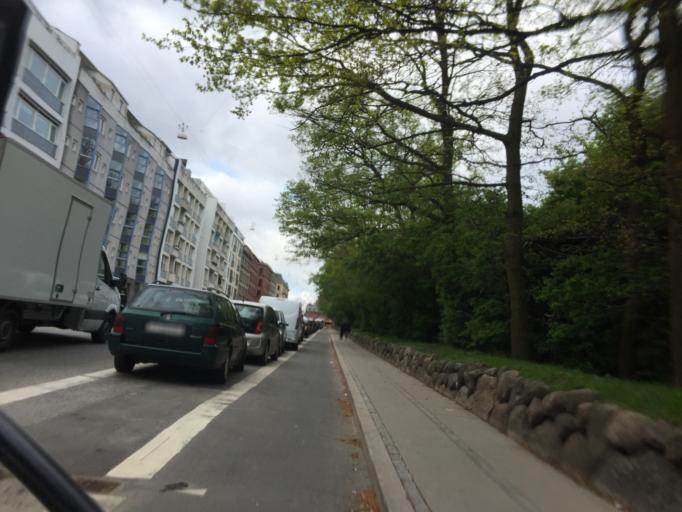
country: DK
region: Capital Region
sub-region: Frederiksberg Kommune
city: Frederiksberg
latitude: 55.6703
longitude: 12.5309
